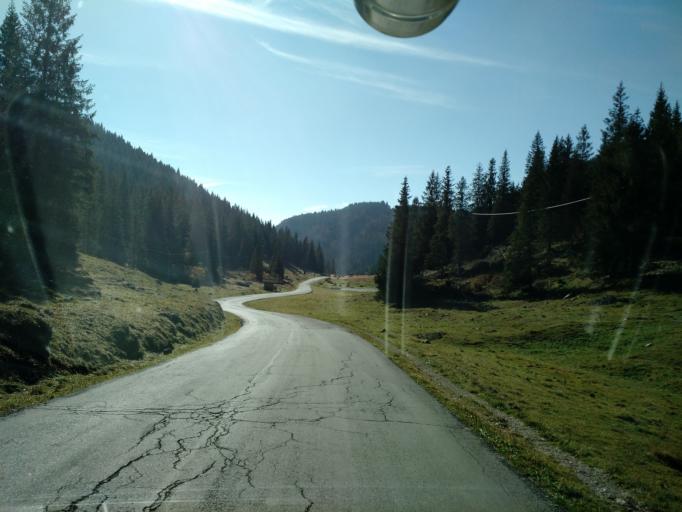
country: IT
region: Veneto
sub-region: Provincia di Vicenza
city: Gallio
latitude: 45.9278
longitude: 11.5600
